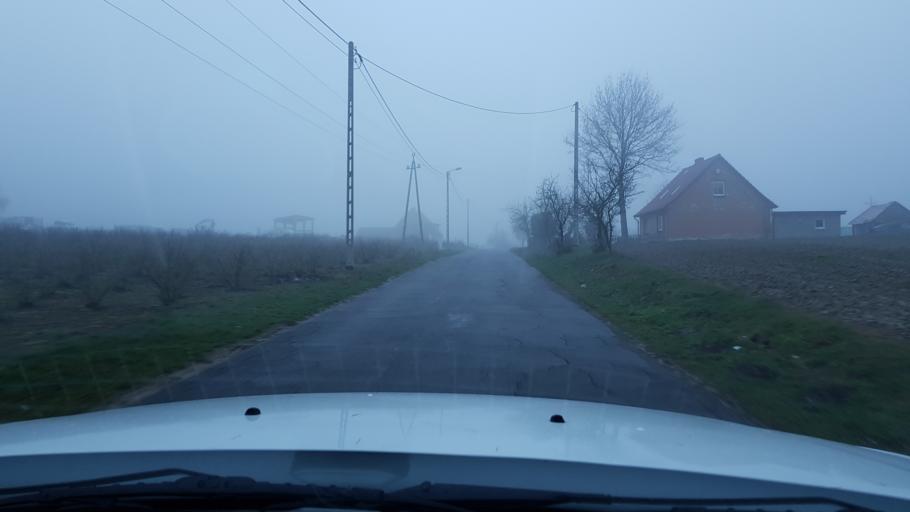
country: PL
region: West Pomeranian Voivodeship
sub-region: Powiat mysliborski
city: Mysliborz
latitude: 52.9074
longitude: 14.8206
